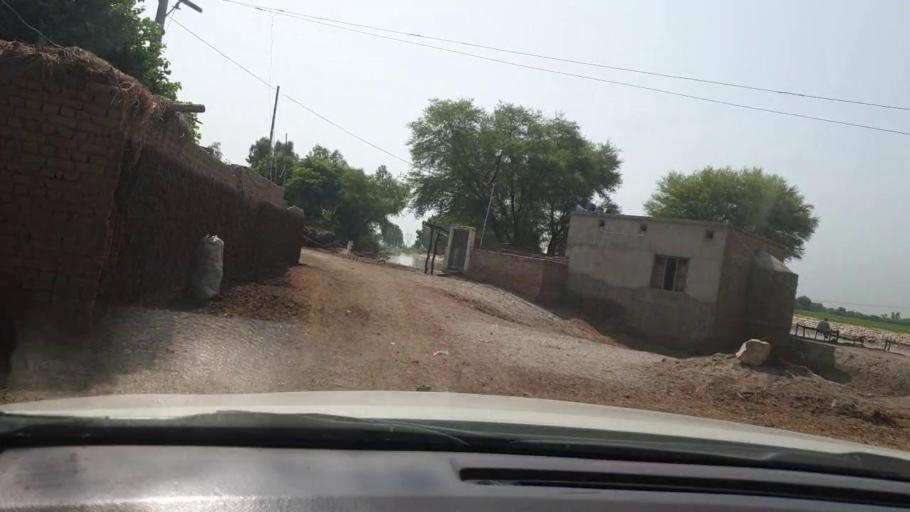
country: PK
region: Sindh
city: Rustam jo Goth
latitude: 27.9729
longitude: 68.7788
